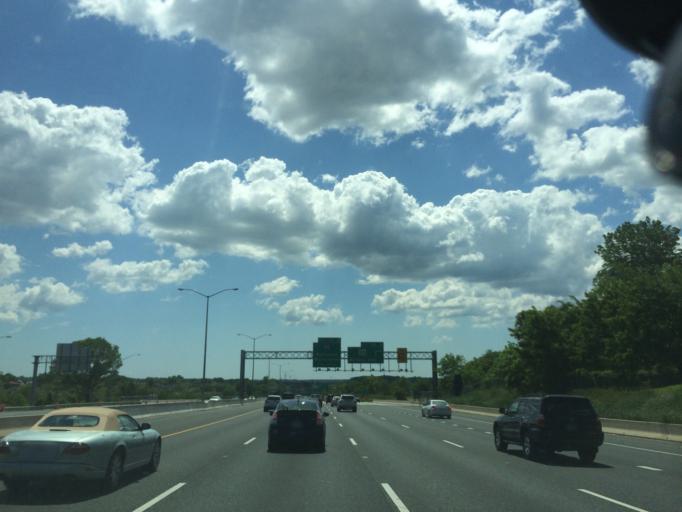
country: US
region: Maryland
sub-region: Baltimore County
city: Charlestown
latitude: 39.2633
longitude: -76.7086
